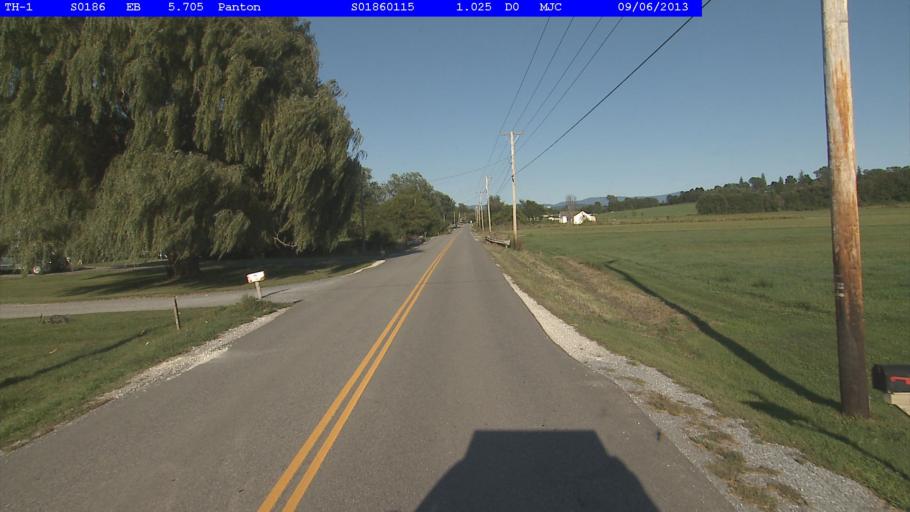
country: US
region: Vermont
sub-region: Addison County
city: Vergennes
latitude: 44.1605
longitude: -73.2759
